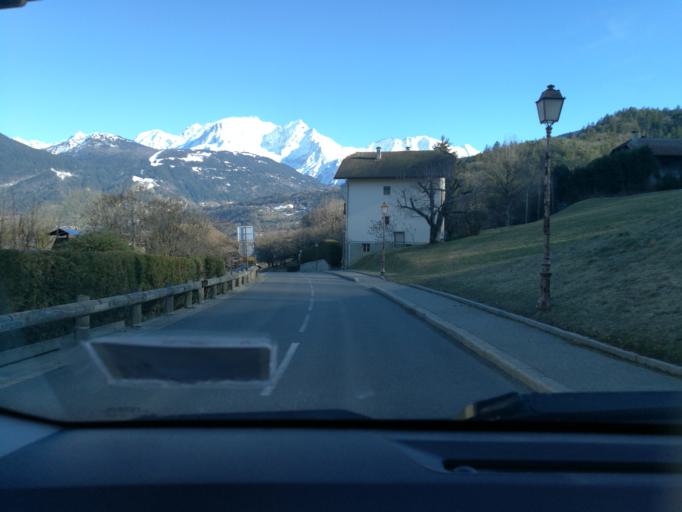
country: FR
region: Rhone-Alpes
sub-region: Departement de la Haute-Savoie
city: Domancy
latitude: 45.9120
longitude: 6.6499
